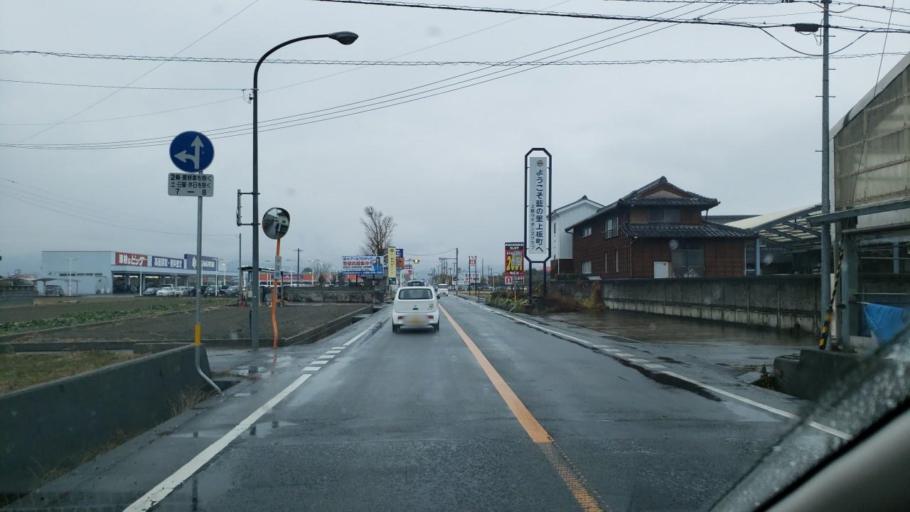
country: JP
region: Tokushima
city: Ishii
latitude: 34.1112
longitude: 134.4365
